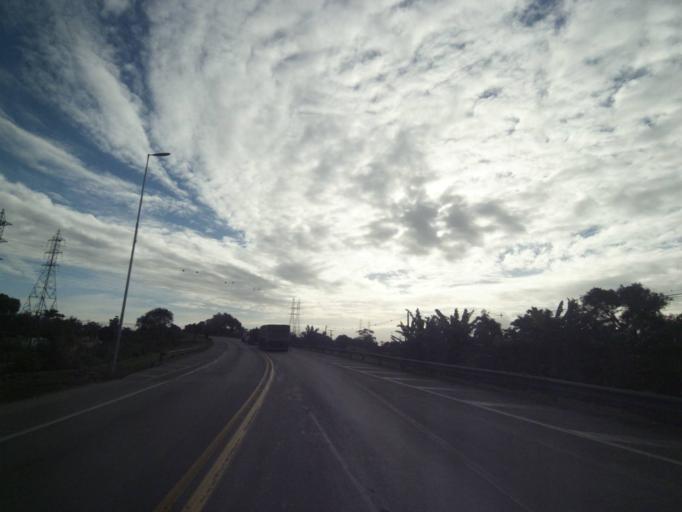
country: BR
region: Parana
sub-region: Paranagua
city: Paranagua
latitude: -25.5541
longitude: -48.5627
